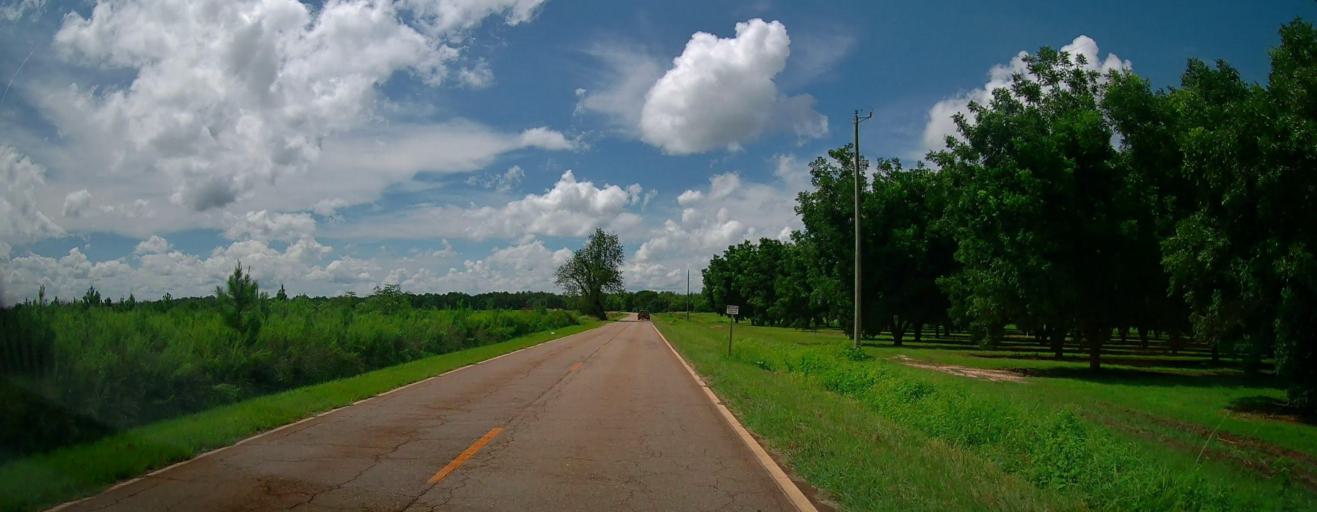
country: US
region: Georgia
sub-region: Houston County
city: Perry
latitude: 32.5220
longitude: -83.7636
